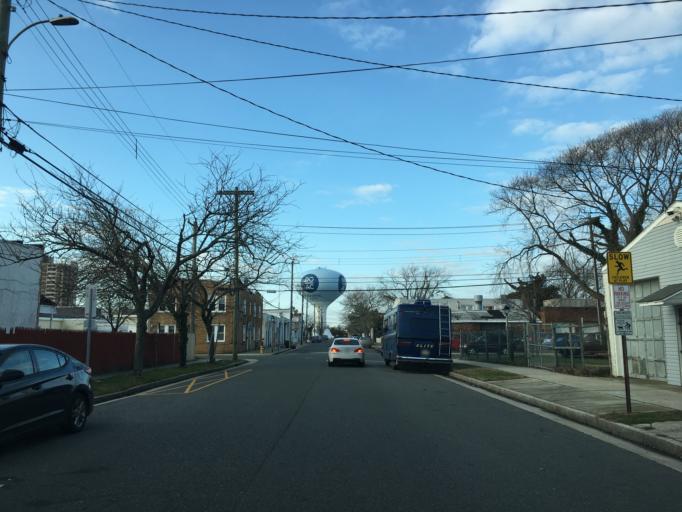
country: US
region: New Jersey
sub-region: Atlantic County
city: Atlantic City
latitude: 39.3714
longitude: -74.4225
